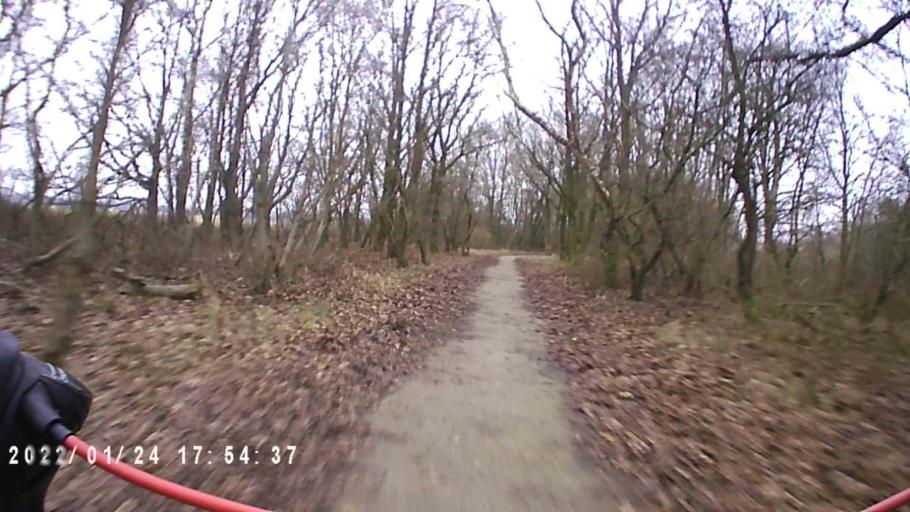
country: NL
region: Groningen
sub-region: Gemeente De Marne
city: Ulrum
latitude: 53.4036
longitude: 6.2335
